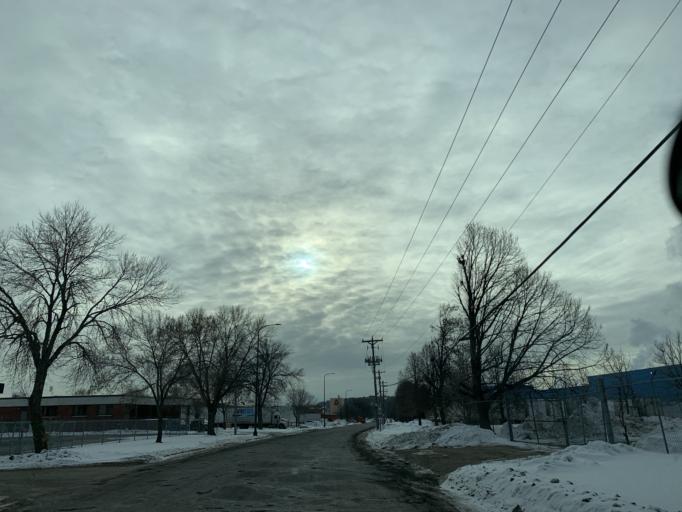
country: US
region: Minnesota
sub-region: Ramsey County
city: Saint Paul
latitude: 44.9423
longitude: -93.0822
